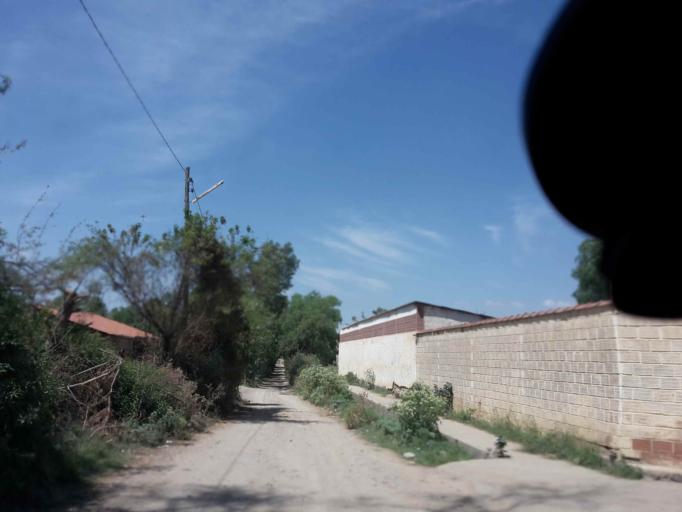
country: BO
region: Cochabamba
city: Cochabamba
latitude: -17.3607
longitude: -66.2222
